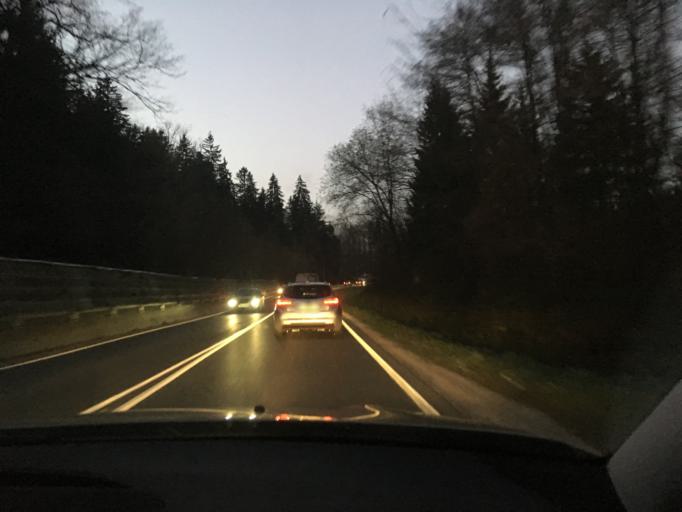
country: SI
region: Domzale
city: Vir
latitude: 46.1368
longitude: 14.6131
